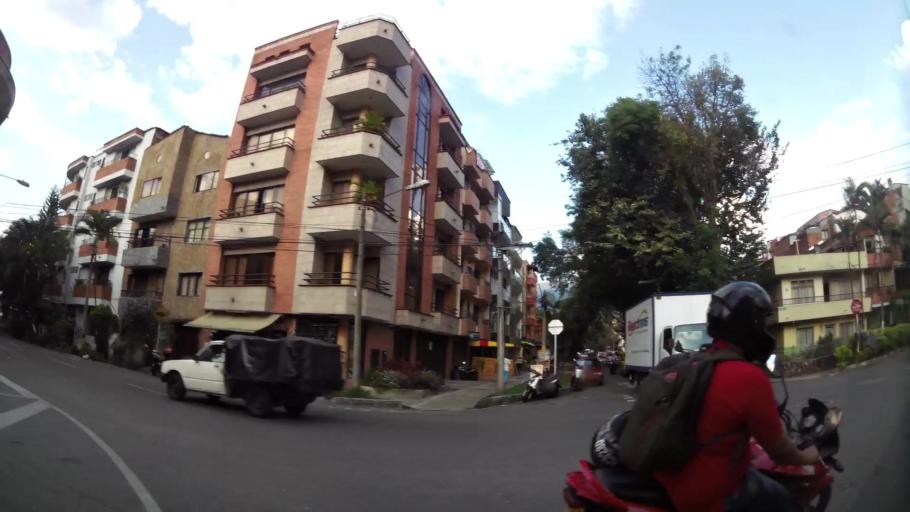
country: CO
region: Antioquia
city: Envigado
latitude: 6.1708
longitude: -75.5847
